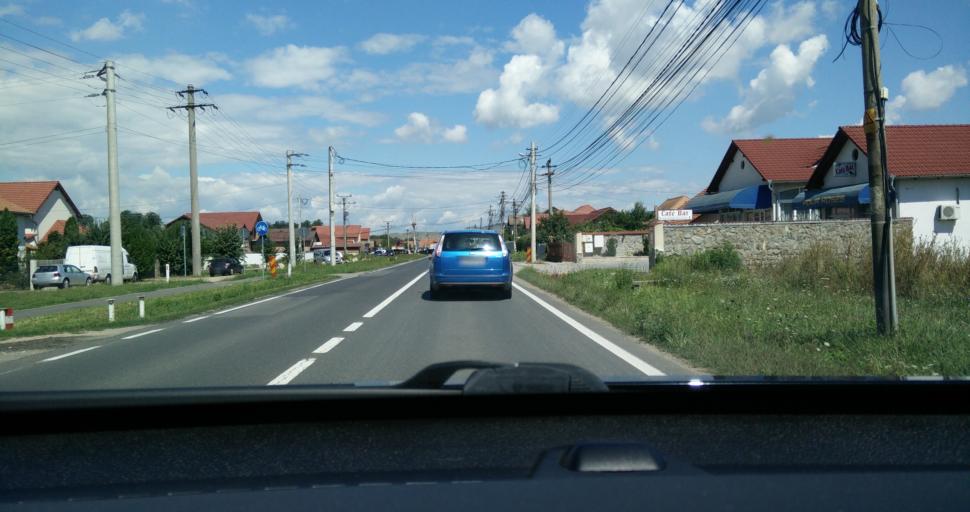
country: RO
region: Alba
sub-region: Municipiul Sebes
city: Sebes
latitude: 45.9399
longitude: 23.5629
